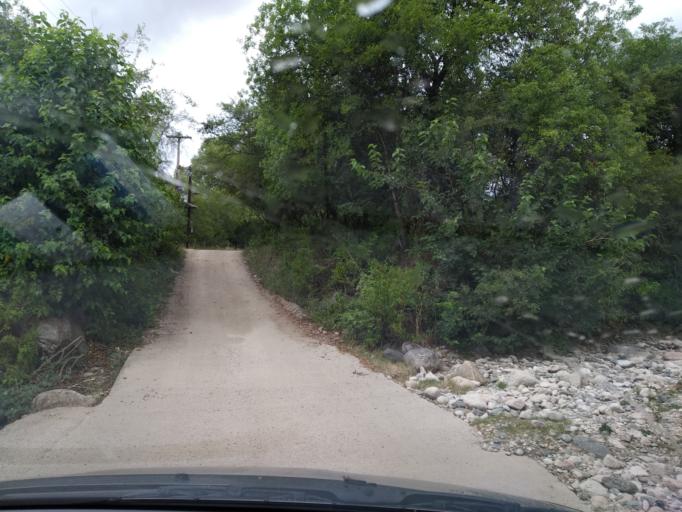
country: AR
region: Cordoba
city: Villa Las Rosas
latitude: -31.9440
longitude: -65.0349
